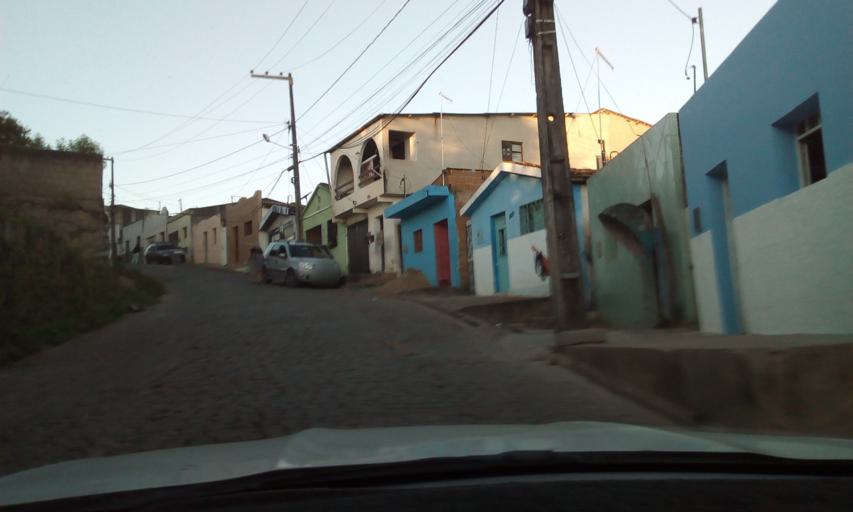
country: BR
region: Paraiba
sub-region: Areia
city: Areia
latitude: -6.9714
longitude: -35.7048
